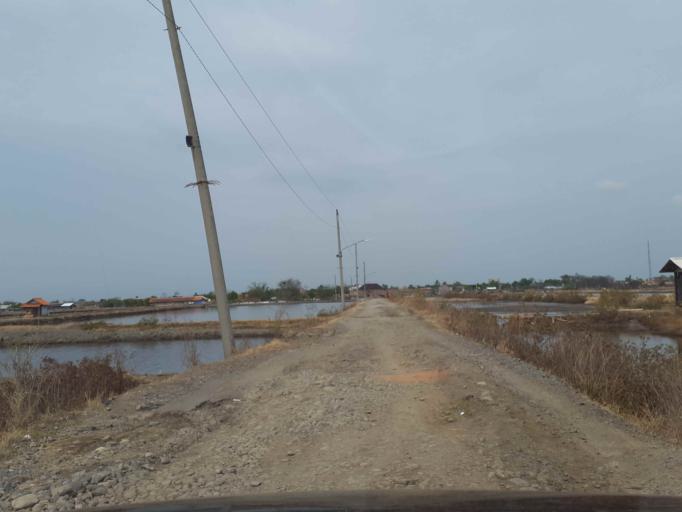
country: ID
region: Central Java
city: Bulakamba
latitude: -6.8480
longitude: 108.8820
